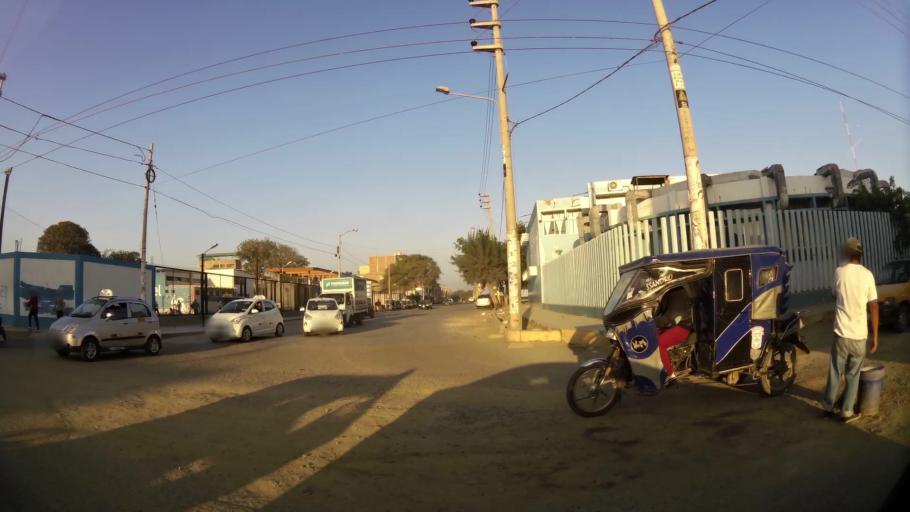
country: PE
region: Lambayeque
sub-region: Provincia de Chiclayo
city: Santa Rosa
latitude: -6.7719
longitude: -79.8320
